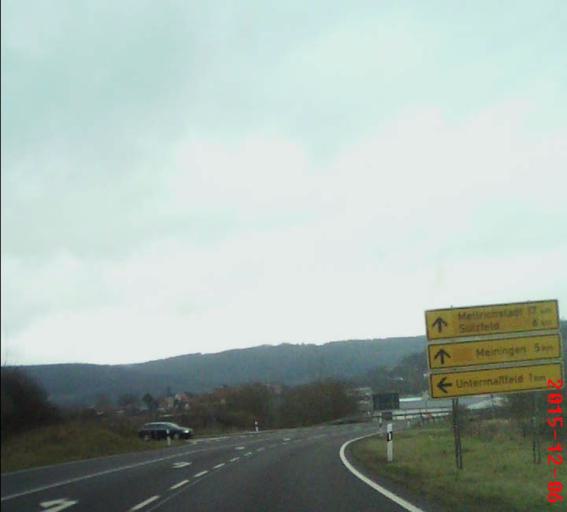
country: DE
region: Thuringia
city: Untermassfeld
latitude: 50.5236
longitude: 10.4260
